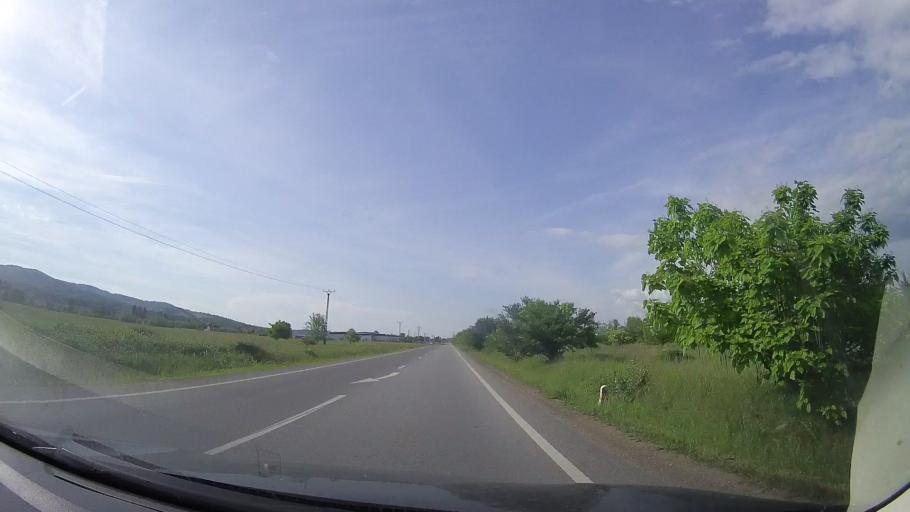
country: RO
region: Caras-Severin
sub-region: Comuna Buchin
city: Buchin
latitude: 45.3762
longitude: 22.2353
